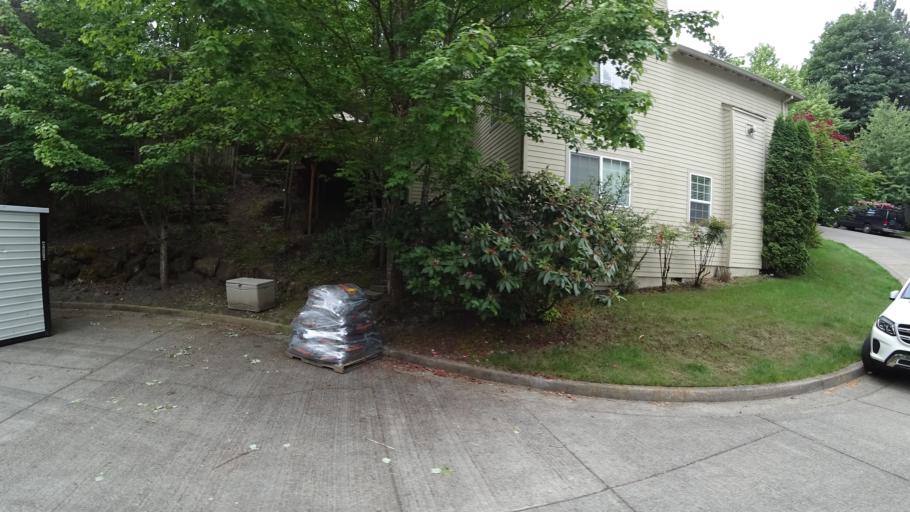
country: US
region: Oregon
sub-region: Clackamas County
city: Lake Oswego
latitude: 45.4446
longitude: -122.7042
